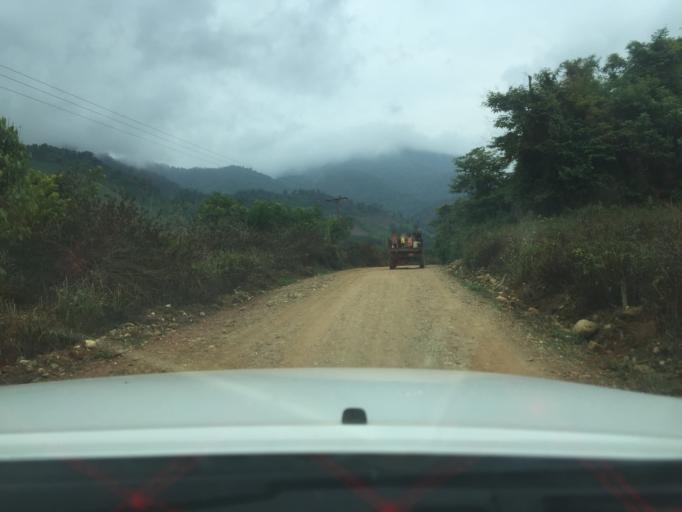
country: TH
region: Phayao
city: Phu Sang
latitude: 19.7417
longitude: 100.4412
